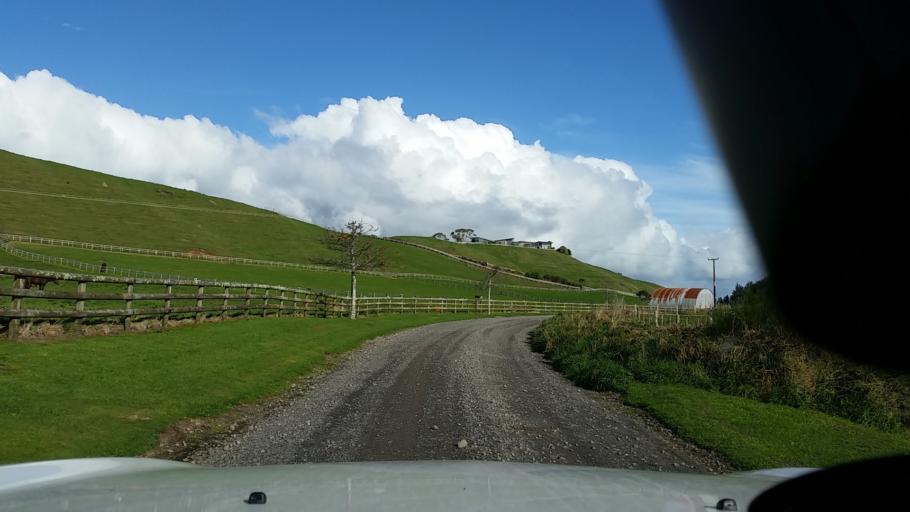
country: NZ
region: Bay of Plenty
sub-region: Rotorua District
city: Rotorua
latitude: -38.0241
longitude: 176.2842
